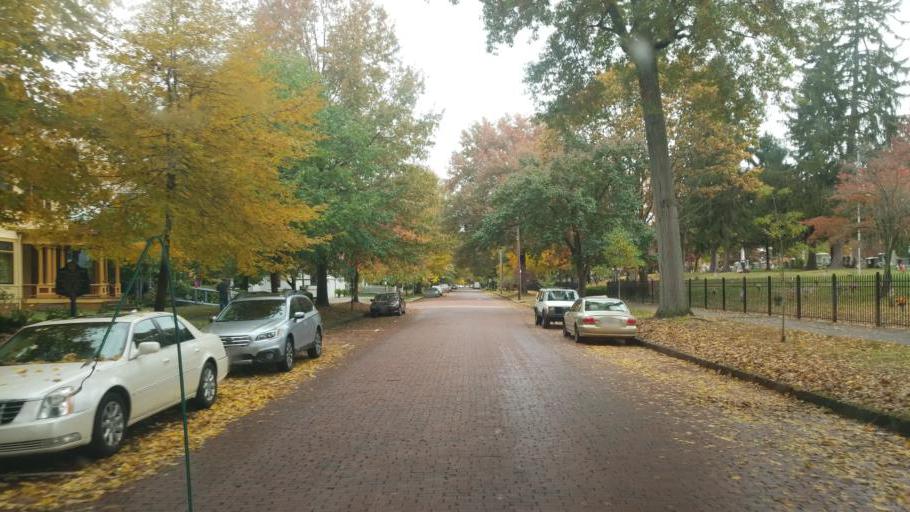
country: US
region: Ohio
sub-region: Washington County
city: Marietta
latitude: 39.4193
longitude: -81.4522
